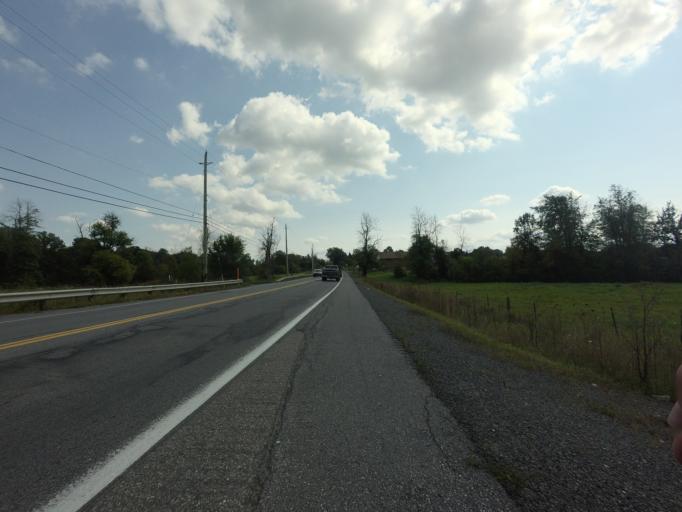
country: CA
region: Ontario
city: Bells Corners
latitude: 45.2307
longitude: -75.6930
